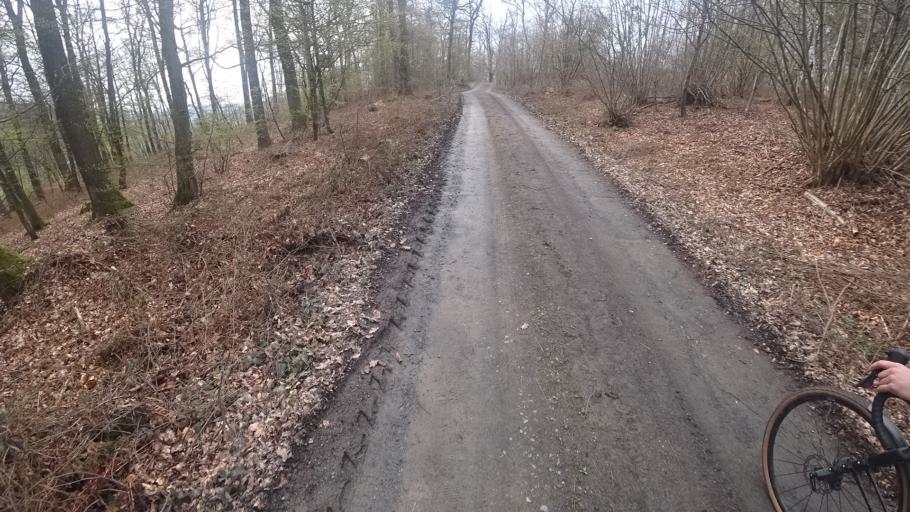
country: DE
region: Rheinland-Pfalz
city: Scheuerfeld
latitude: 50.7802
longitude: 7.8257
